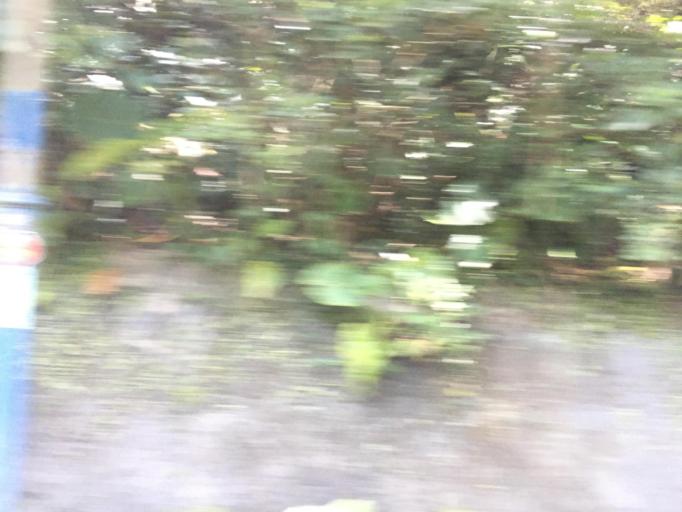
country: TW
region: Taiwan
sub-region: Yilan
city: Yilan
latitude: 24.8165
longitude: 121.7338
